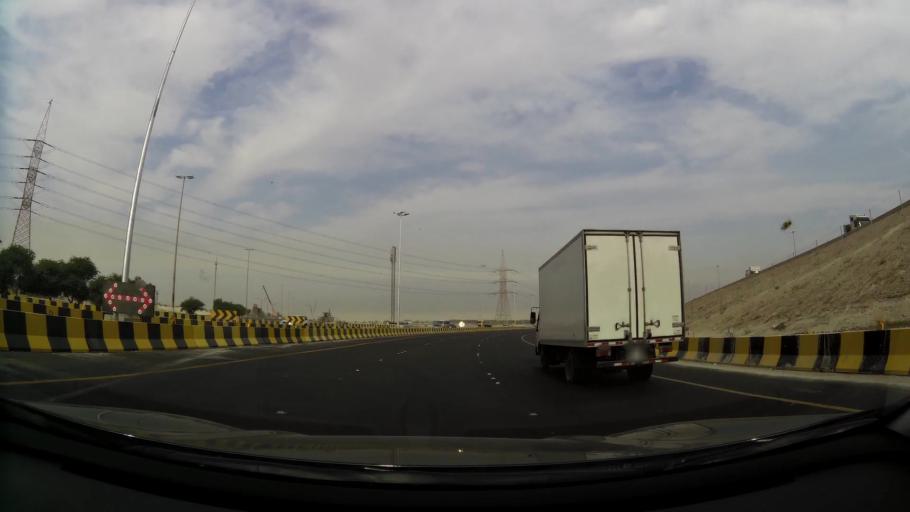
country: KW
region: Al Asimah
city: Ar Rabiyah
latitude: 29.2820
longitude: 47.7905
